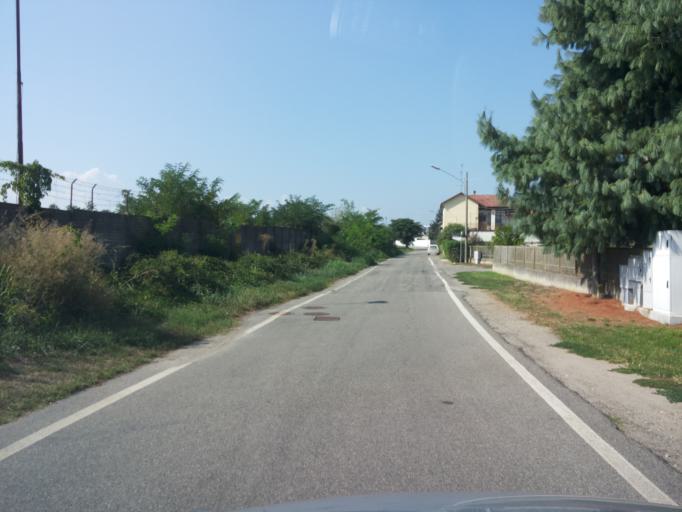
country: IT
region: Piedmont
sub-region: Provincia di Vercelli
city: Vercelli
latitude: 45.3086
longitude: 8.4329
